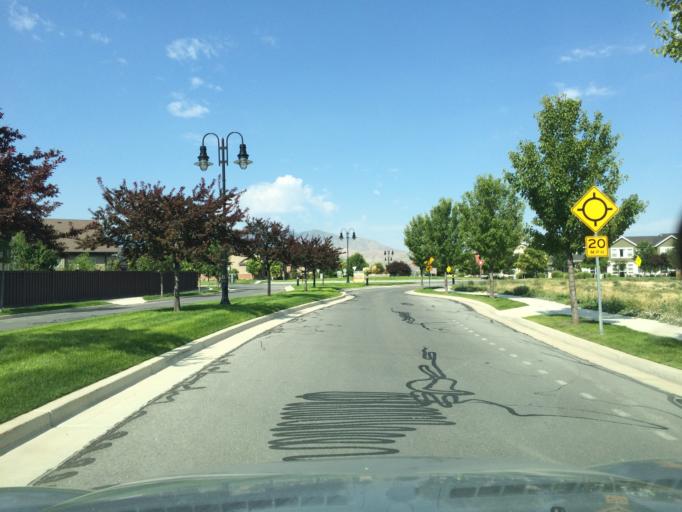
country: US
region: Utah
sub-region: Salt Lake County
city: West Valley City
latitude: 40.7081
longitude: -112.0189
